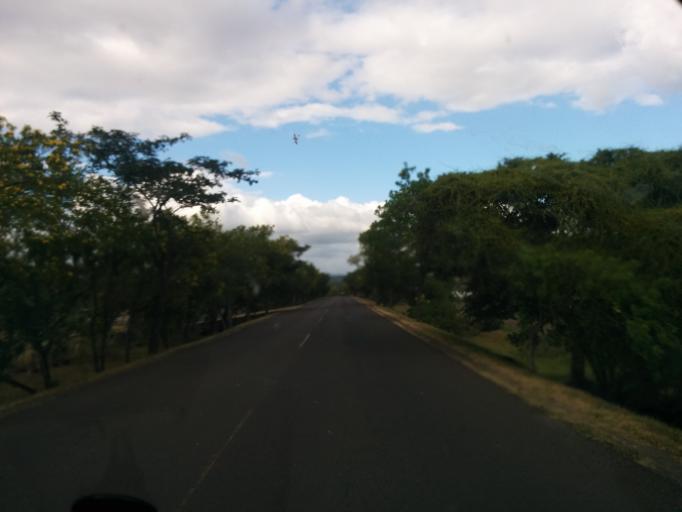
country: NI
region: Esteli
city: Esteli
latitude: 13.1690
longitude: -86.3672
